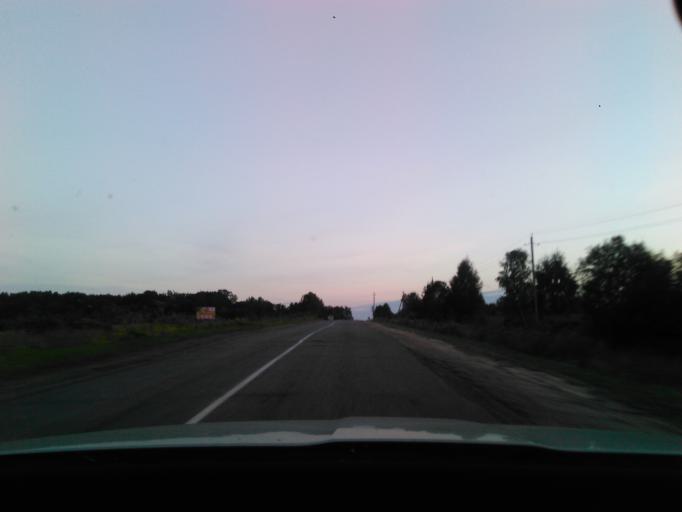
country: RU
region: Moskovskaya
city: Klin
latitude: 56.2171
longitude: 36.7303
